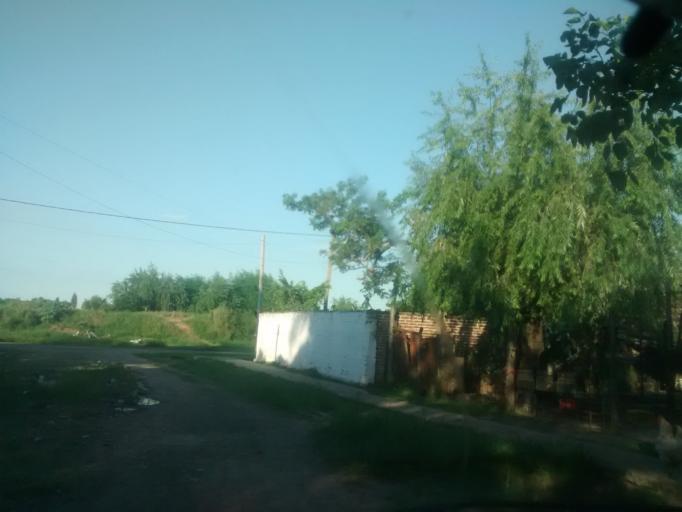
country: AR
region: Chaco
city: Fontana
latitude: -27.4389
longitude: -59.0101
